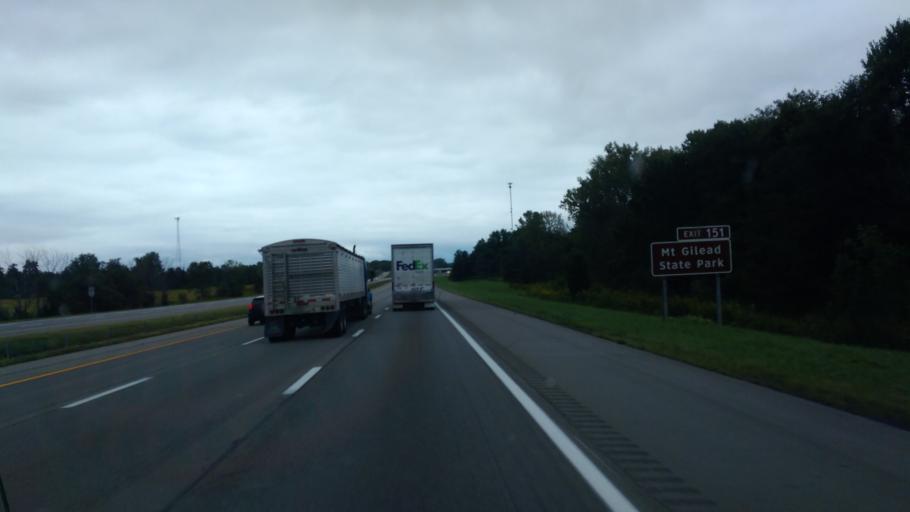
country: US
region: Ohio
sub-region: Morrow County
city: Mount Gilead
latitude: 40.4910
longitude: -82.7264
